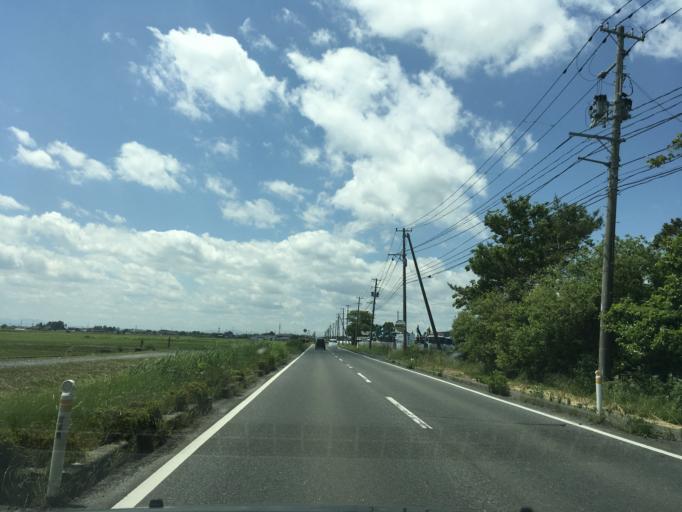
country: JP
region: Miyagi
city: Wakuya
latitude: 38.6785
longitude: 141.2251
